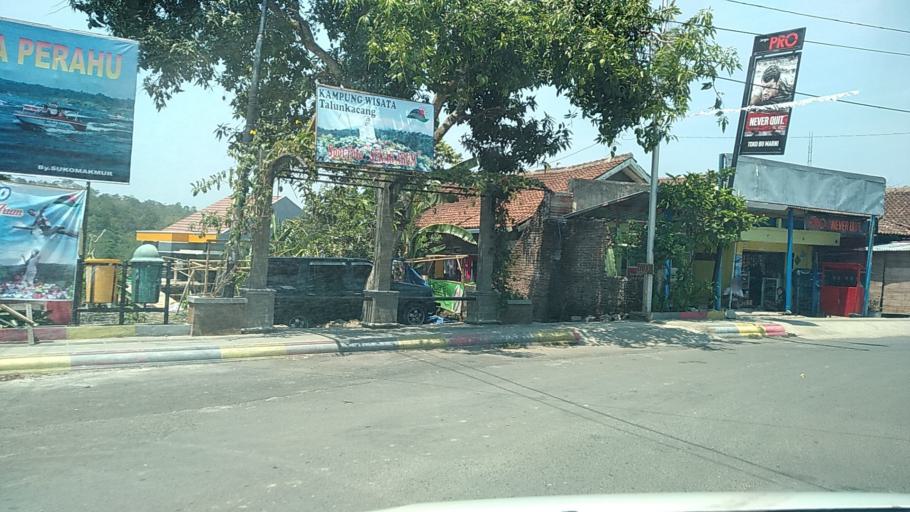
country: ID
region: Central Java
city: Semarang
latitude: -7.0394
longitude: 110.3545
